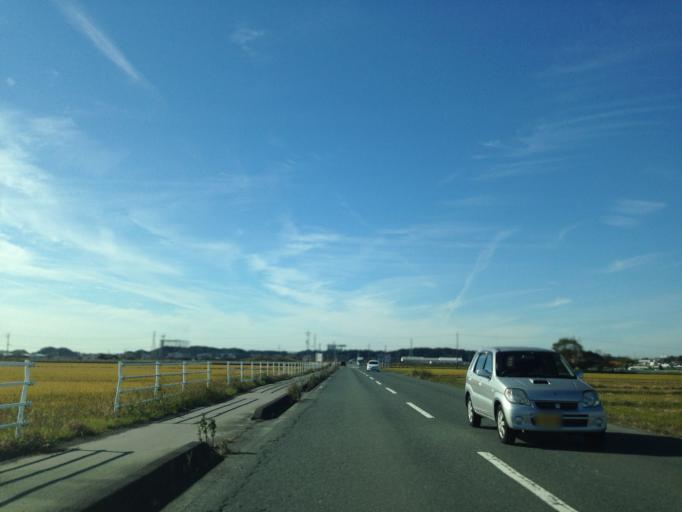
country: JP
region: Shizuoka
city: Fukuroi
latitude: 34.7372
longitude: 137.9063
